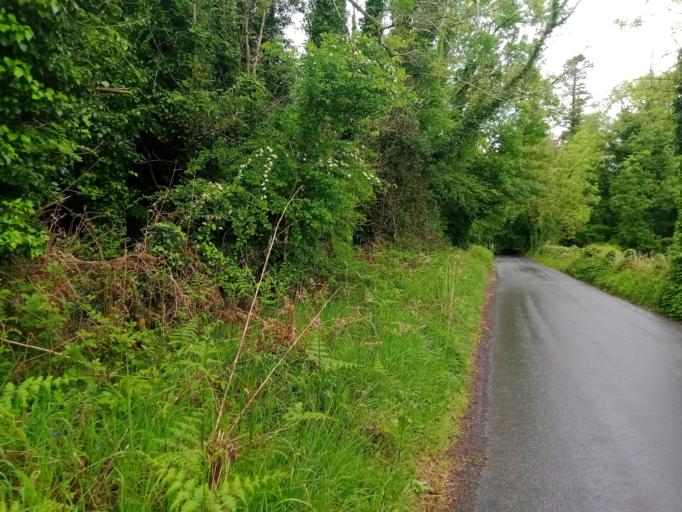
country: IE
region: Leinster
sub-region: Kilkenny
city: Thomastown
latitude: 52.4807
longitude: -7.0653
